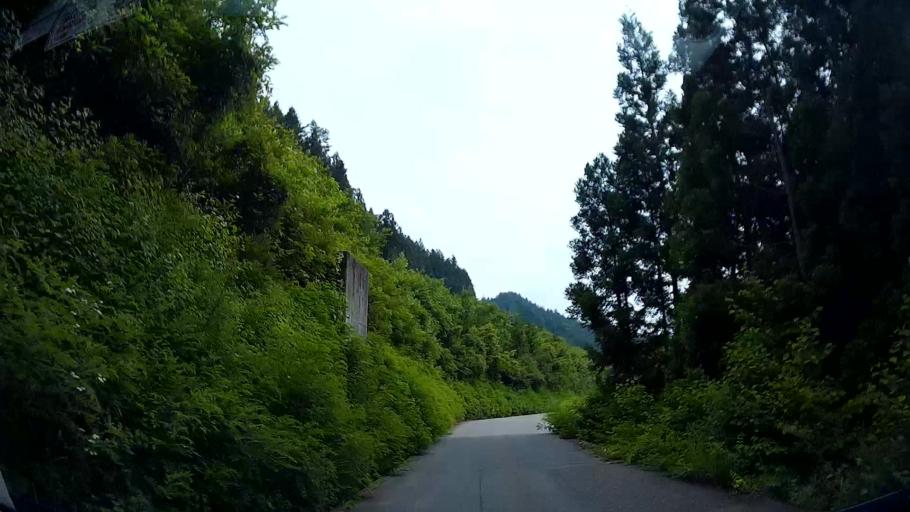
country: JP
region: Nagano
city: Iida
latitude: 35.4488
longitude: 137.9962
